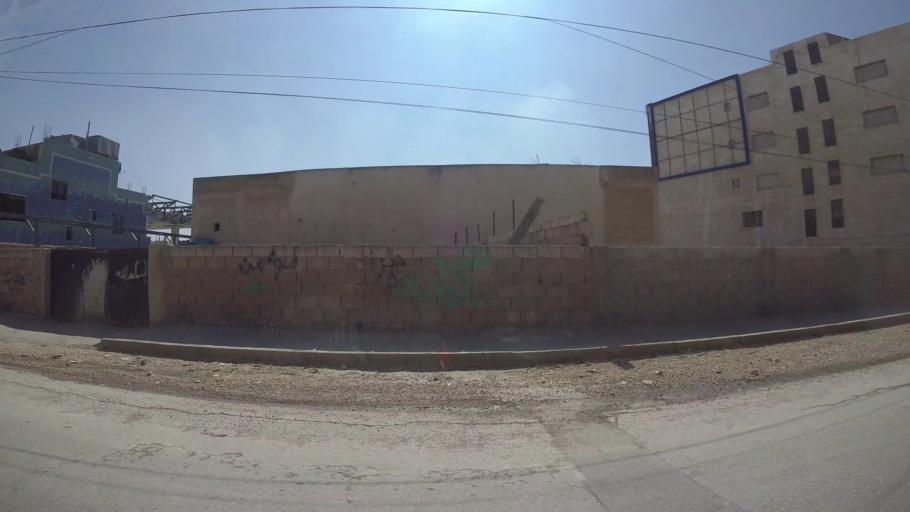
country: JO
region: Amman
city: Al Bunayyat ash Shamaliyah
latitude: 31.8992
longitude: 35.8984
